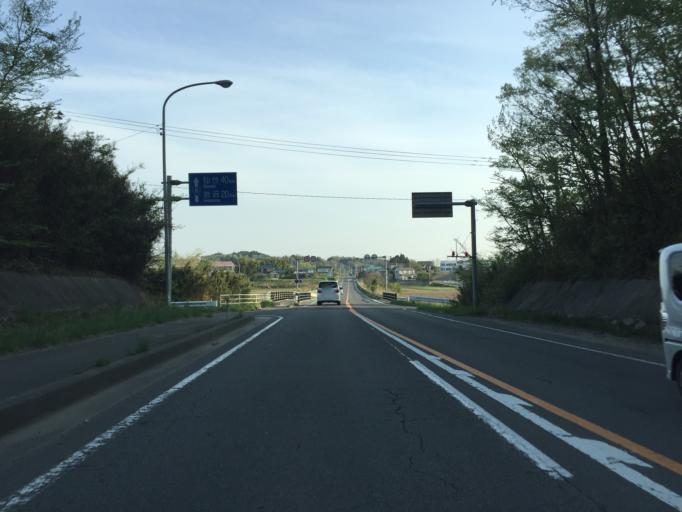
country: JP
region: Miyagi
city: Watari
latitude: 37.9364
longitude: 140.8941
